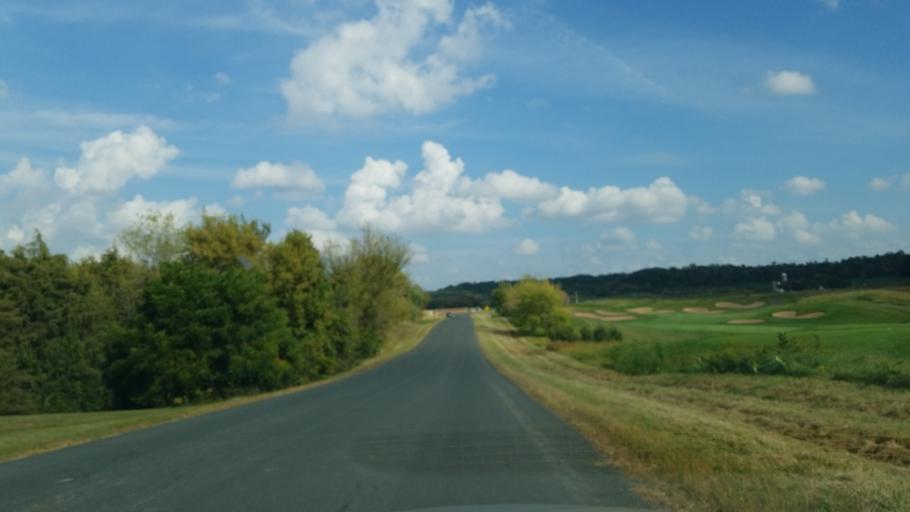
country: US
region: Minnesota
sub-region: Washington County
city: Lake Saint Croix Beach
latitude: 44.9056
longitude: -92.7357
